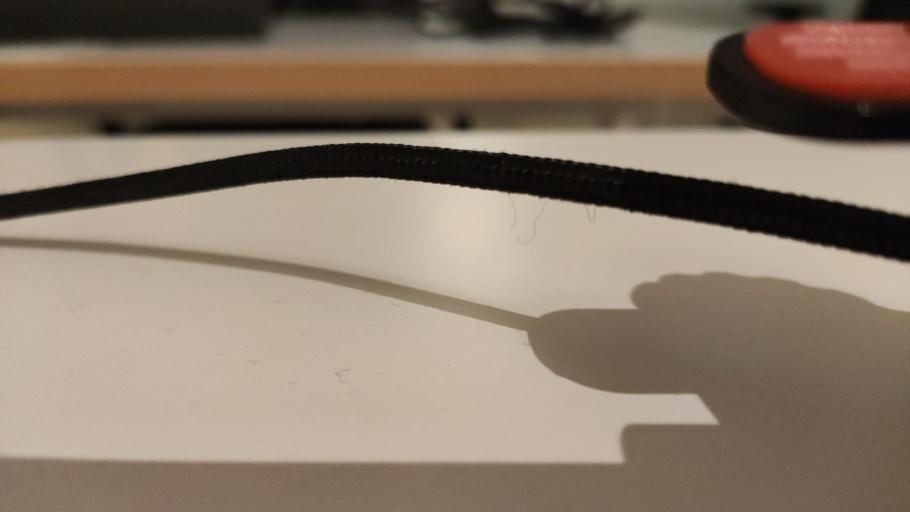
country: RU
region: Moskovskaya
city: Semkhoz
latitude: 56.3847
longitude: 38.0633
